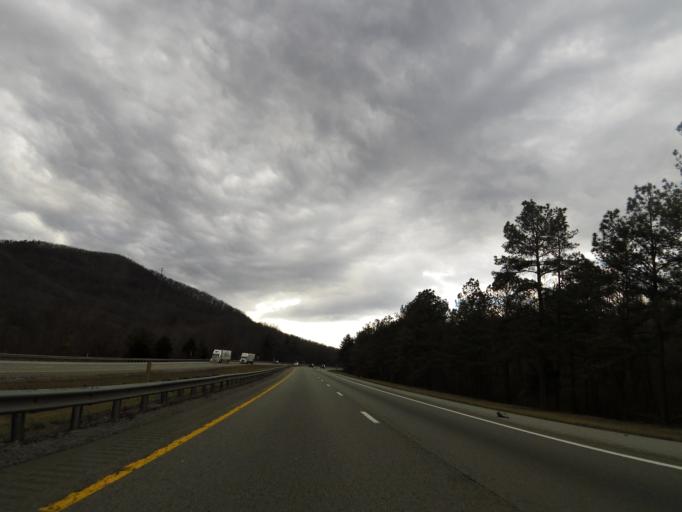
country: US
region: Tennessee
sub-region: Cumberland County
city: Fairfield Glade
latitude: 35.8981
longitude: -84.8464
